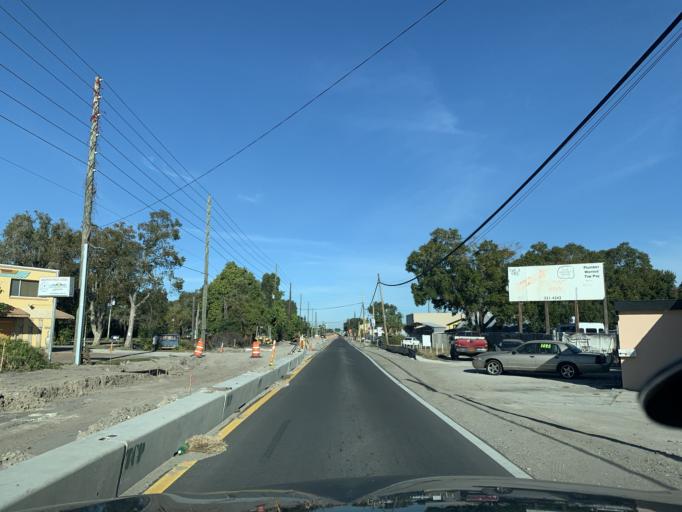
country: US
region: Florida
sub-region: Pinellas County
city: Lealman
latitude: 27.8304
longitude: -82.6774
